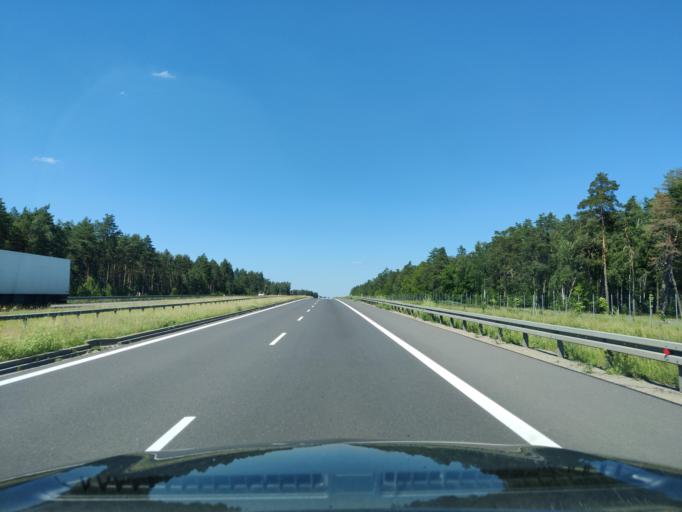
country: PL
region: Masovian Voivodeship
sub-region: Powiat mlawski
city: Wieczfnia Koscielna
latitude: 53.2440
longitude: 20.4244
